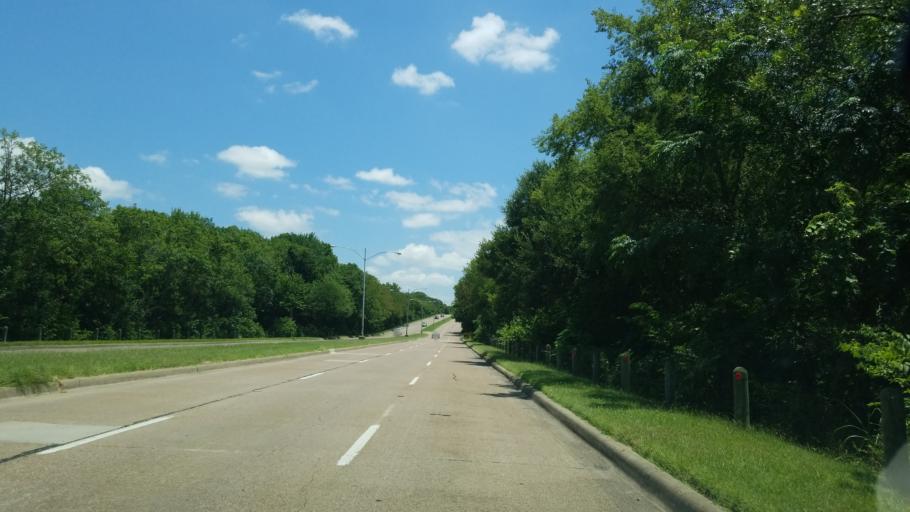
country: US
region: Texas
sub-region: Dallas County
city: Balch Springs
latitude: 32.7492
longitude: -96.7097
